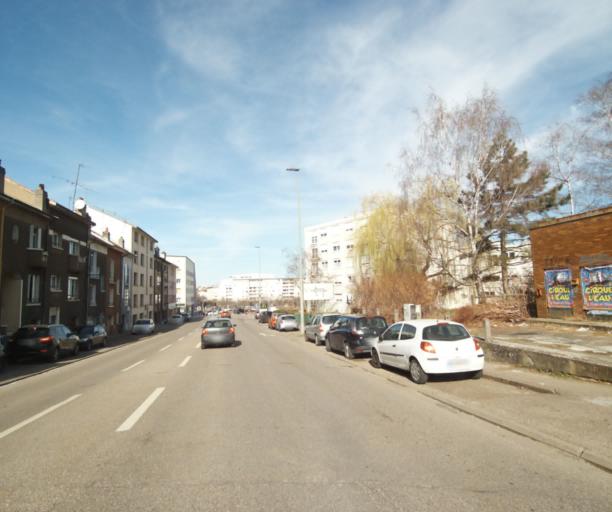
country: FR
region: Lorraine
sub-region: Departement de Meurthe-et-Moselle
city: Villers-les-Nancy
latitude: 48.6646
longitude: 6.1672
